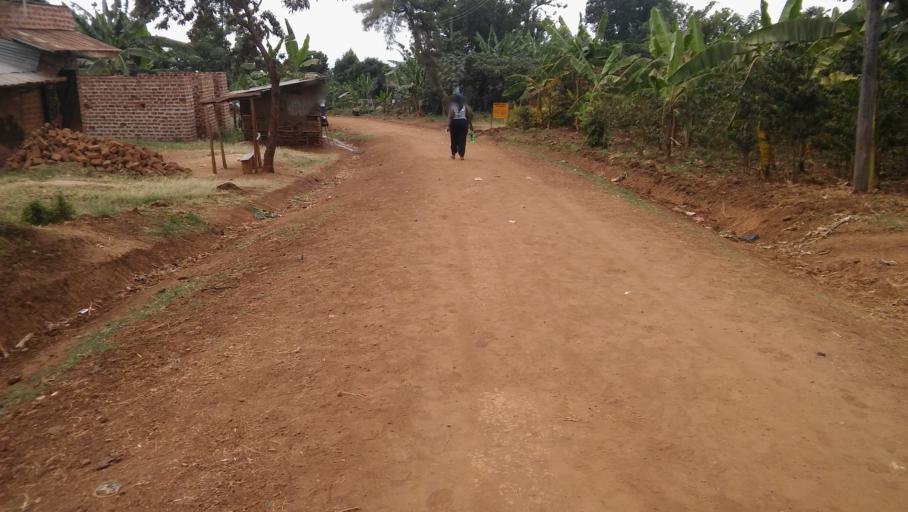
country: UG
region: Eastern Region
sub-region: Mbale District
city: Mbale
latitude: 1.0577
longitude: 34.2169
